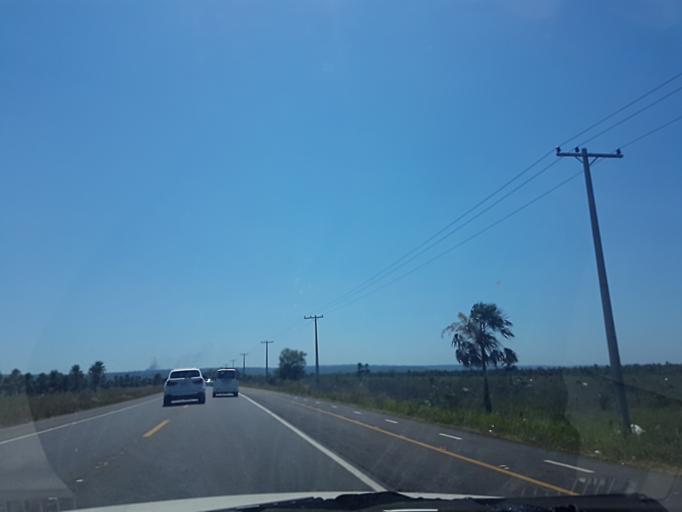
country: PY
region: Cordillera
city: Emboscada
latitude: -25.2092
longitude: -57.3987
